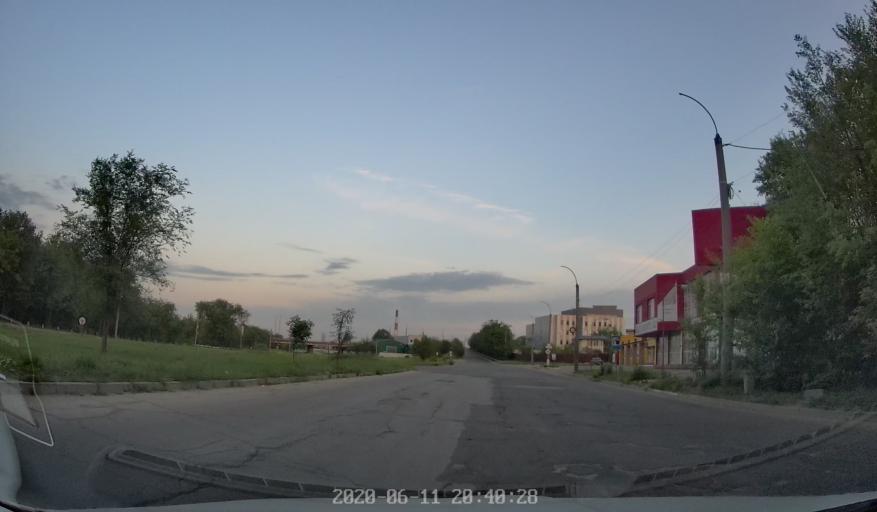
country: MD
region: Chisinau
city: Chisinau
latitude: 46.9863
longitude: 28.9023
